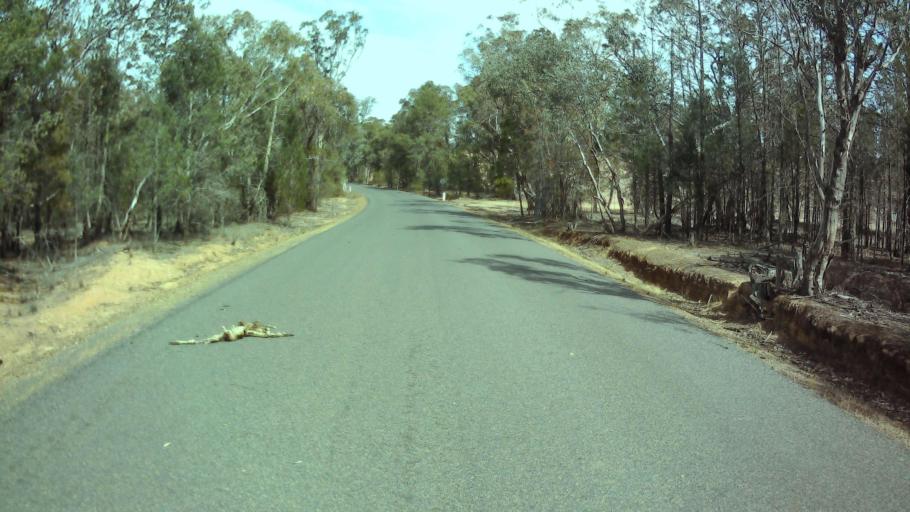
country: AU
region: New South Wales
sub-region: Weddin
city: Grenfell
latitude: -33.8039
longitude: 148.0294
